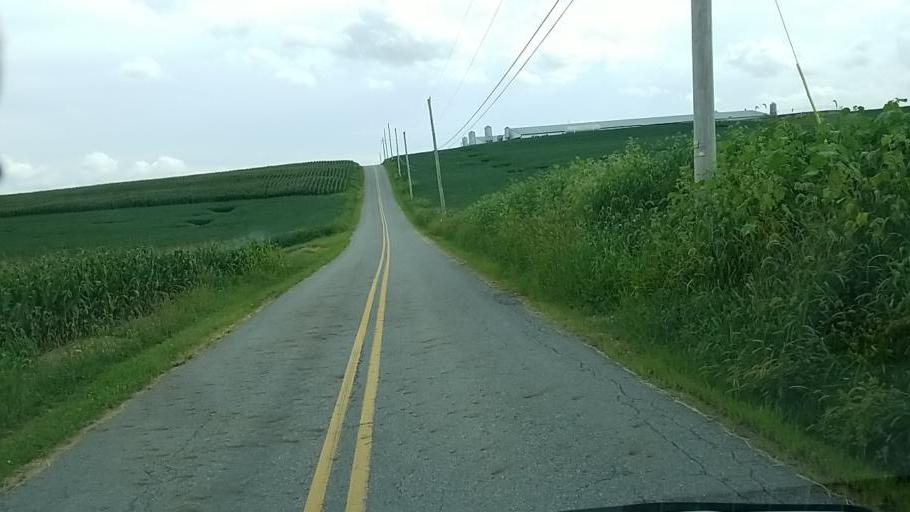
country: US
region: Pennsylvania
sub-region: Dauphin County
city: Elizabethville
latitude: 40.6546
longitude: -76.8351
